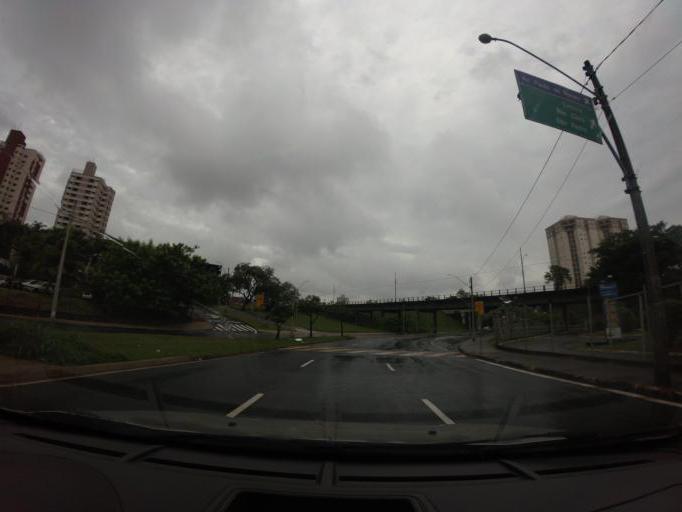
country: BR
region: Sao Paulo
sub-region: Piracicaba
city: Piracicaba
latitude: -22.7384
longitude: -47.6470
